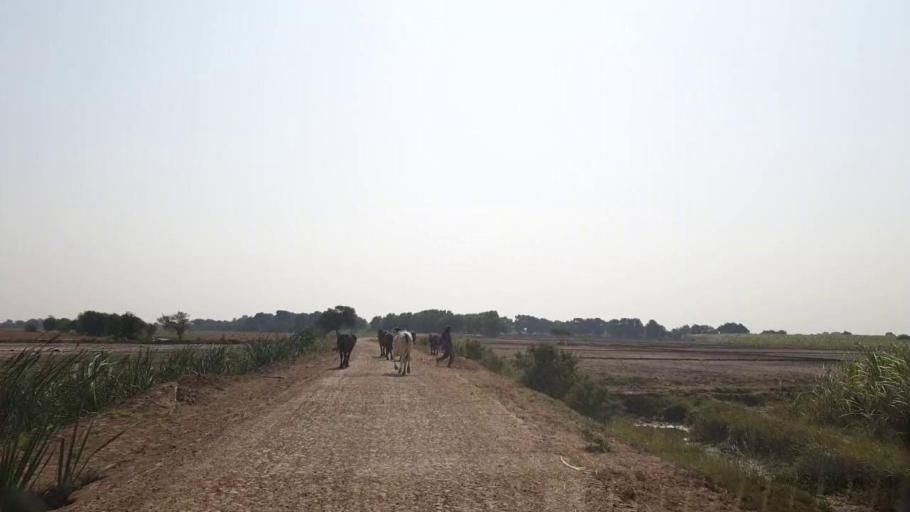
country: PK
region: Sindh
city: Tando Muhammad Khan
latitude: 25.0191
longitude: 68.4174
